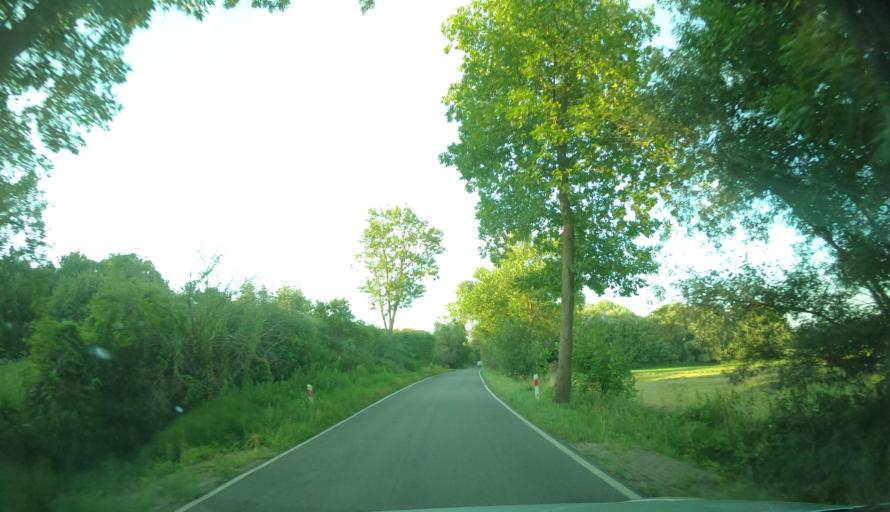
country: PL
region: Kujawsko-Pomorskie
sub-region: Bydgoszcz
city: Fordon
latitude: 53.2237
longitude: 18.1912
